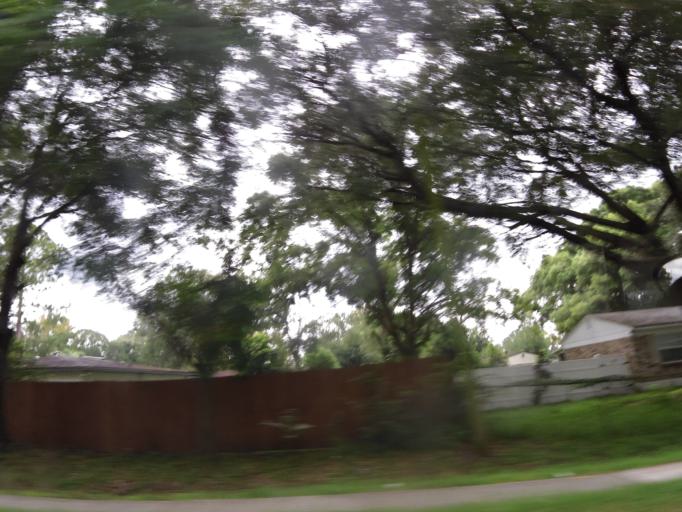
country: US
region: Florida
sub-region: Clay County
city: Bellair-Meadowbrook Terrace
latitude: 30.2535
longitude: -81.7731
